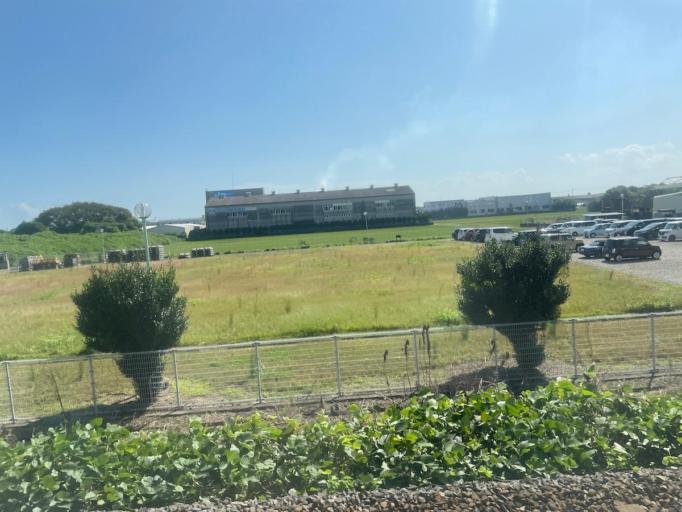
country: JP
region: Mie
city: Kawage
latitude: 34.8071
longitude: 136.5639
